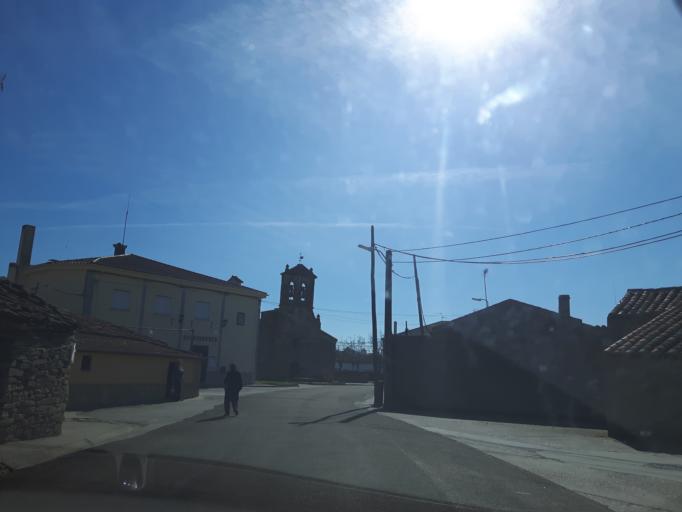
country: ES
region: Castille and Leon
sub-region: Provincia de Salamanca
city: Villar de Peralonso
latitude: 41.0325
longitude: -6.2228
